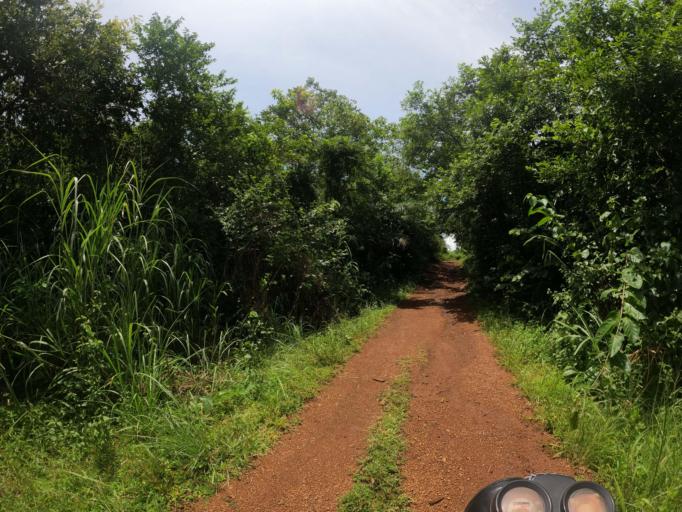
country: SL
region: Northern Province
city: Binkolo
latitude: 9.1548
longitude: -12.1943
